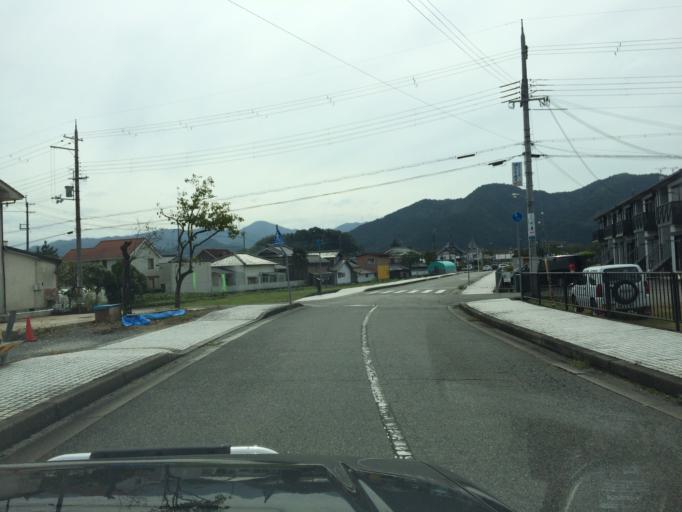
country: JP
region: Hyogo
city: Sasayama
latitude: 35.0711
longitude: 135.2138
